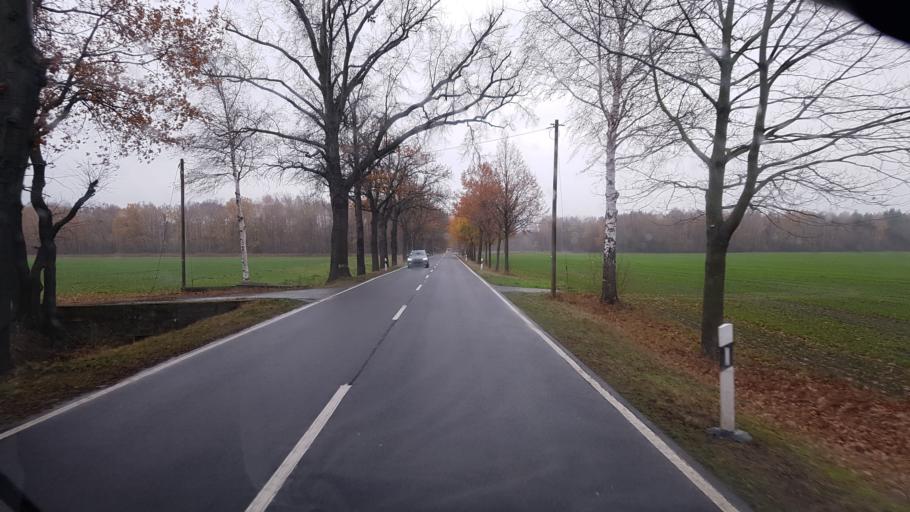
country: DE
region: Brandenburg
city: Schraden
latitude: 51.4475
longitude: 13.7110
